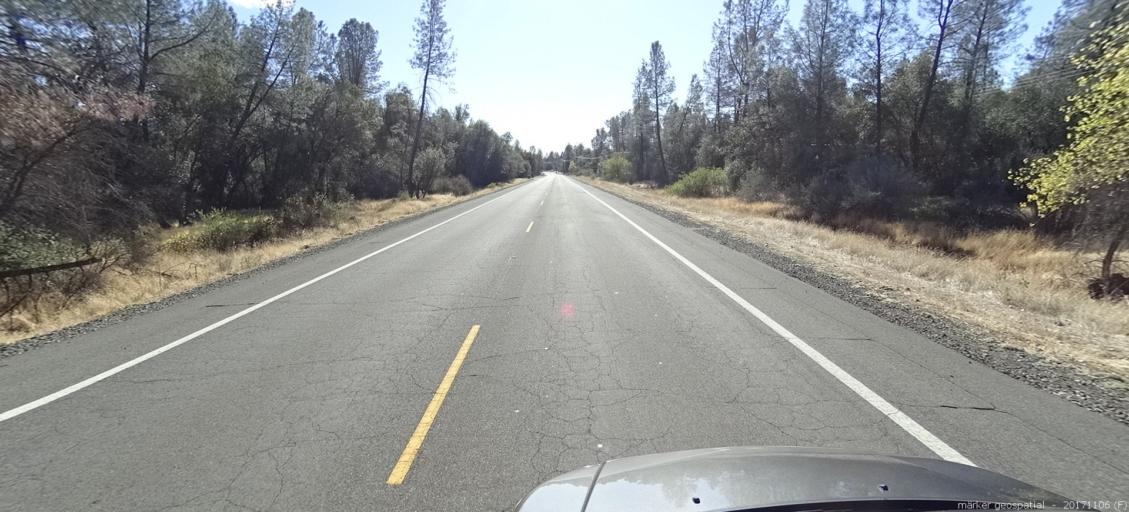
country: US
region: California
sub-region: Shasta County
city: Redding
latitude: 40.6066
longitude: -122.3155
